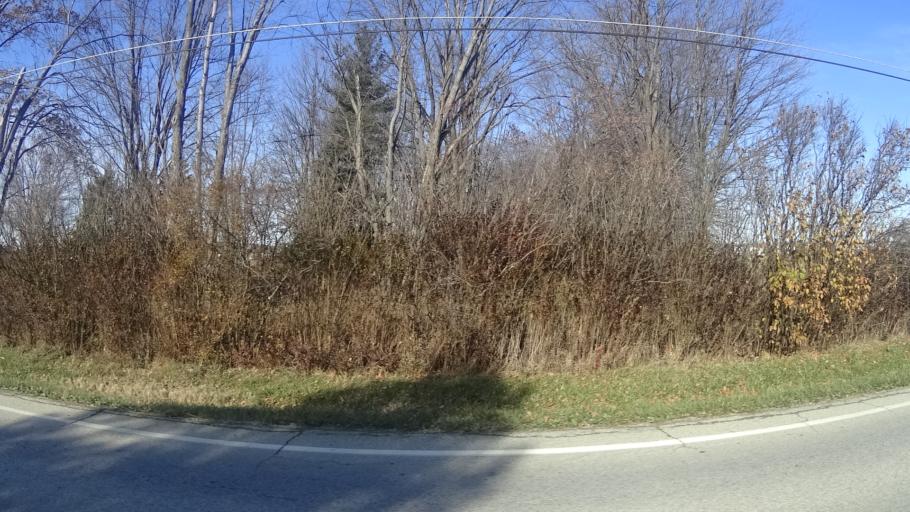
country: US
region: Ohio
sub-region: Lorain County
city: North Ridgeville
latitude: 41.3493
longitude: -82.0428
